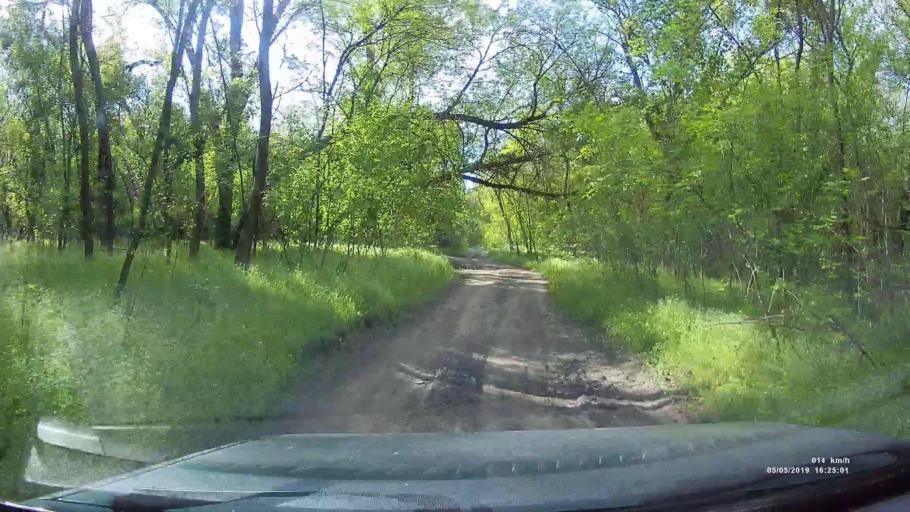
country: RU
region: Rostov
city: Konstantinovsk
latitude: 47.7609
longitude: 41.0242
